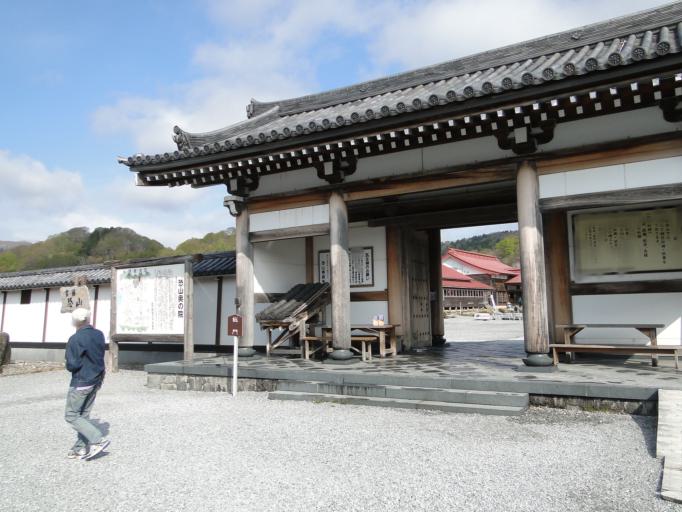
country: JP
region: Aomori
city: Mutsu
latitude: 41.3265
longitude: 141.0908
